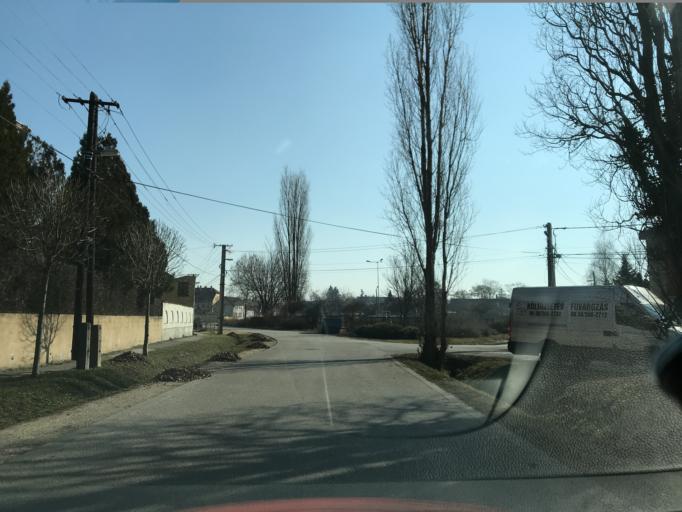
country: HU
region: Gyor-Moson-Sopron
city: Gyor
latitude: 47.6836
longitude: 17.6140
